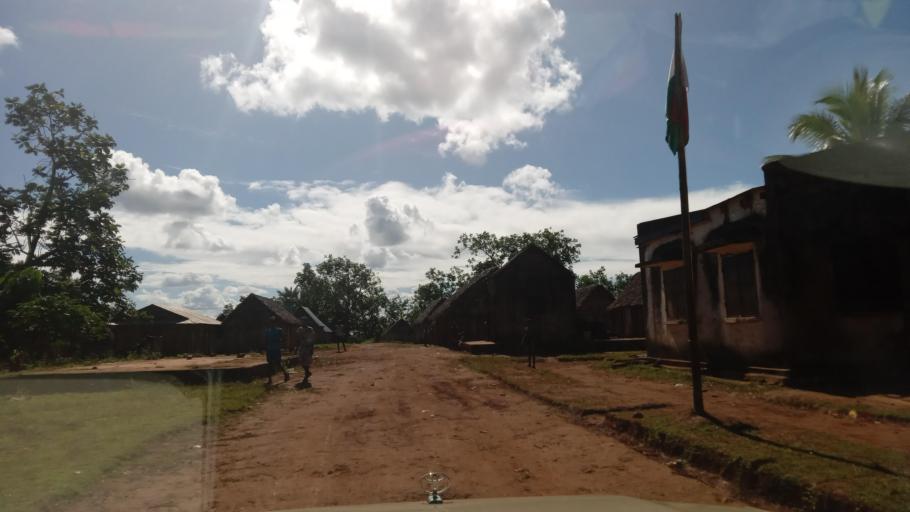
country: MG
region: Atsimo-Atsinanana
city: Vohipaho
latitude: -23.8185
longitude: 47.5488
